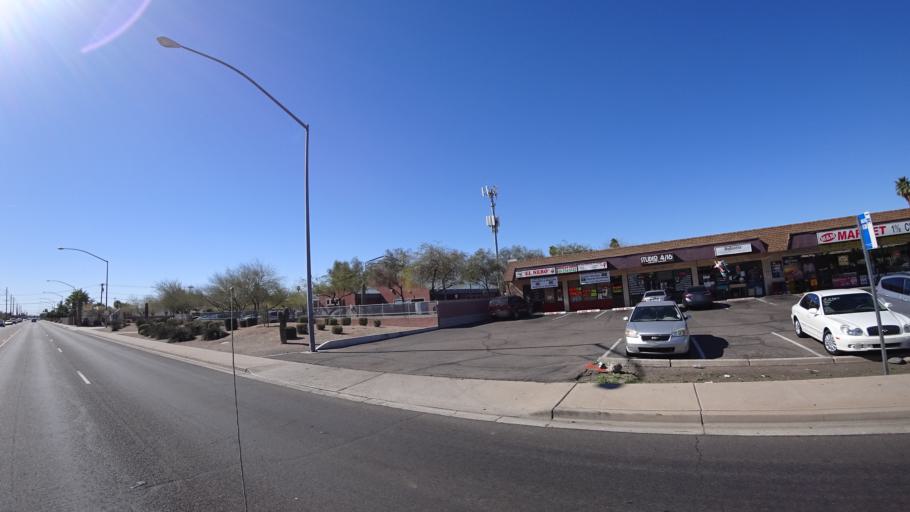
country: US
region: Arizona
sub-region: Maricopa County
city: Mesa
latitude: 33.4003
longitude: -111.8055
